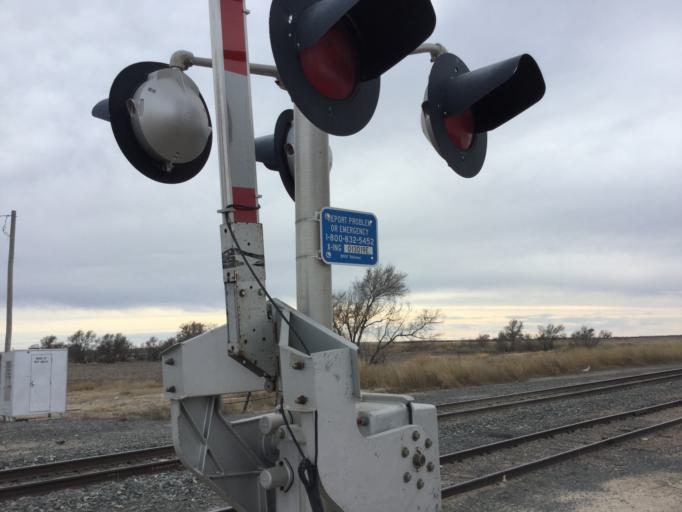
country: US
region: Kansas
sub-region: Hamilton County
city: Syracuse
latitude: 38.0389
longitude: -102.0092
